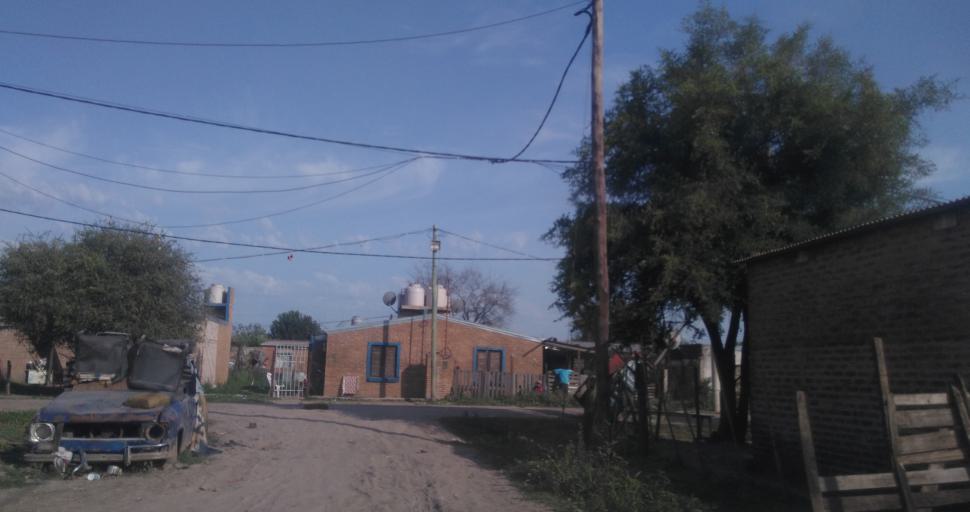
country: AR
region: Chaco
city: Resistencia
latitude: -27.4623
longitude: -59.0194
